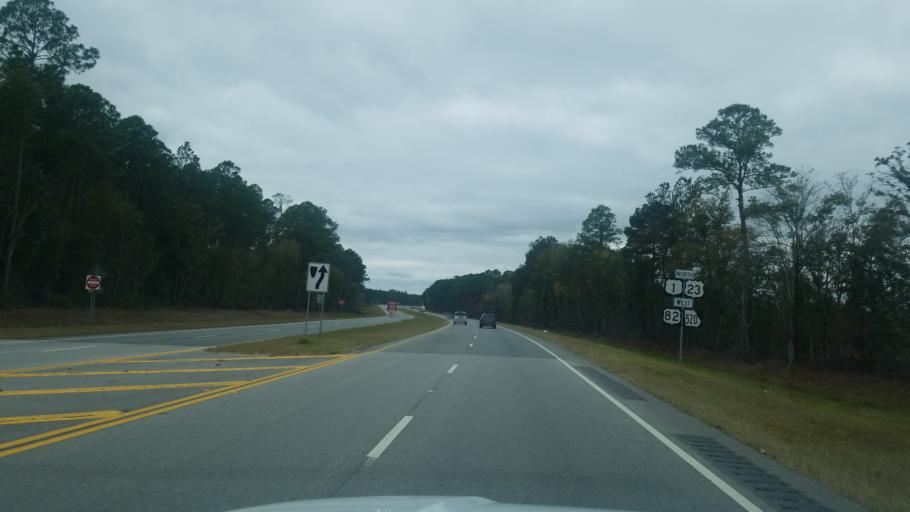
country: US
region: Georgia
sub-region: Ware County
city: Deenwood
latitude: 31.2096
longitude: -82.4025
